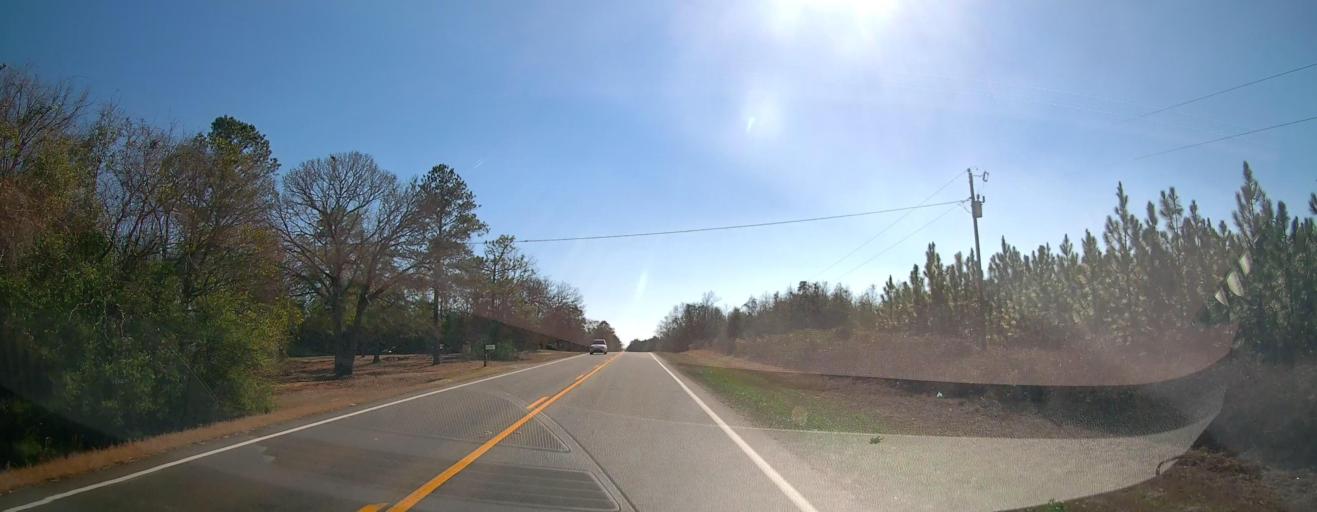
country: US
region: Georgia
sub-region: Macon County
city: Oglethorpe
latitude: 32.2433
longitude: -84.0911
